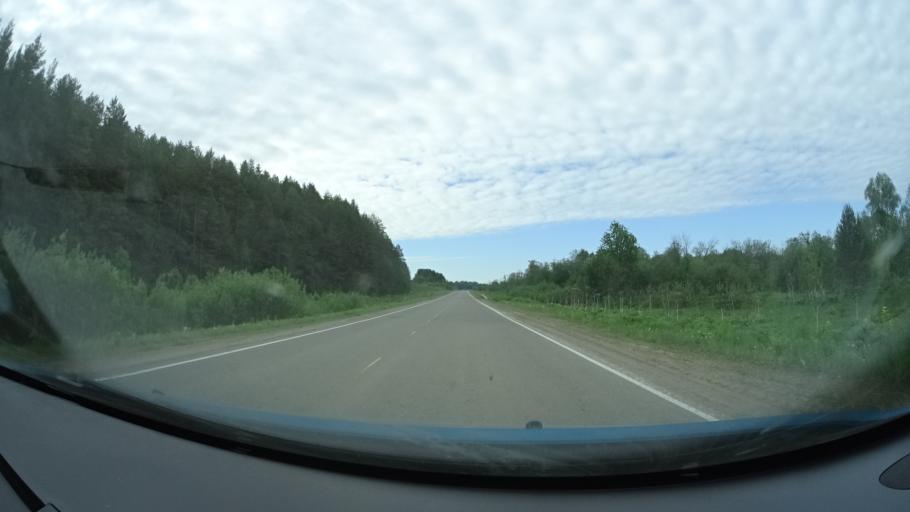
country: RU
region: Perm
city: Kuyeda
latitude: 56.5191
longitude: 55.6258
